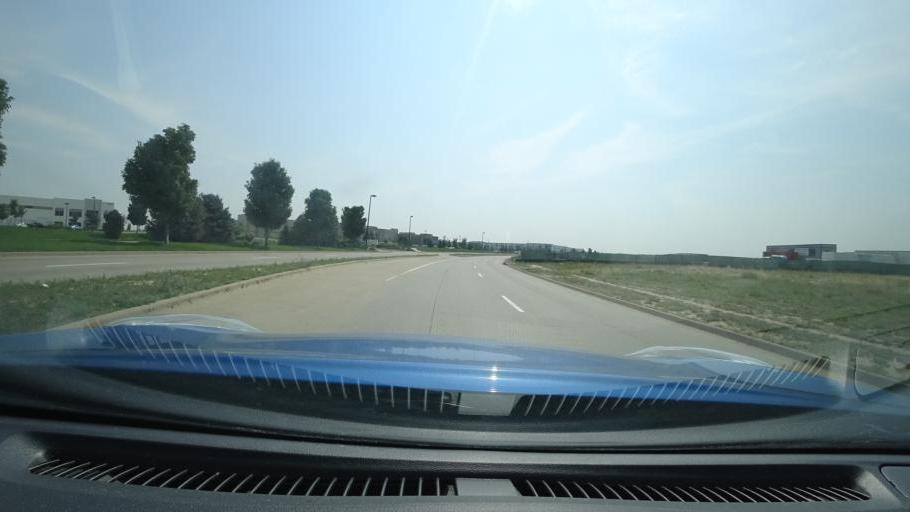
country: US
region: Colorado
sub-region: Adams County
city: Aurora
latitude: 39.7728
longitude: -104.7811
